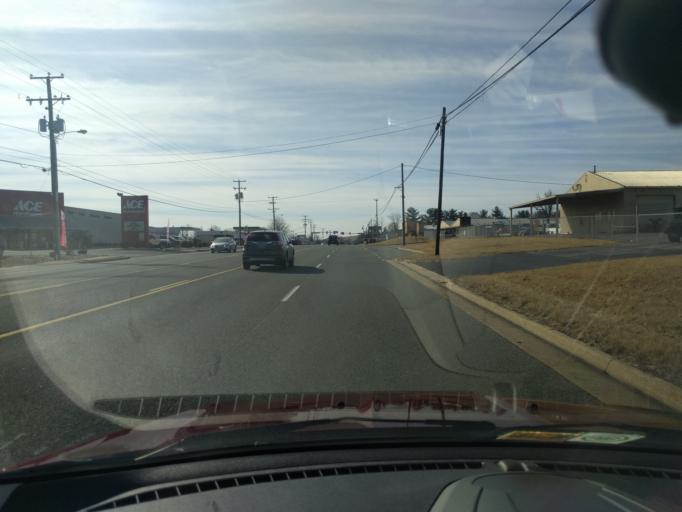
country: US
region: Virginia
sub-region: Augusta County
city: Verona
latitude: 38.1975
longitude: -79.0141
